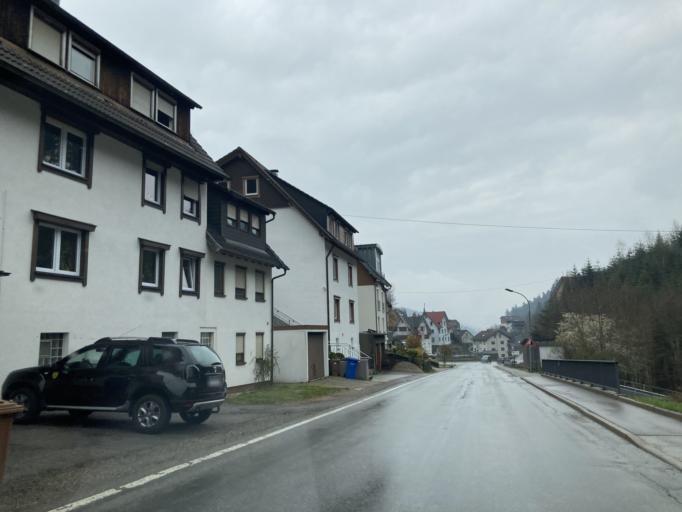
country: DE
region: Baden-Wuerttemberg
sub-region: Freiburg Region
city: Lauterbach/Schwarzwald
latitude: 48.2286
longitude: 8.3354
